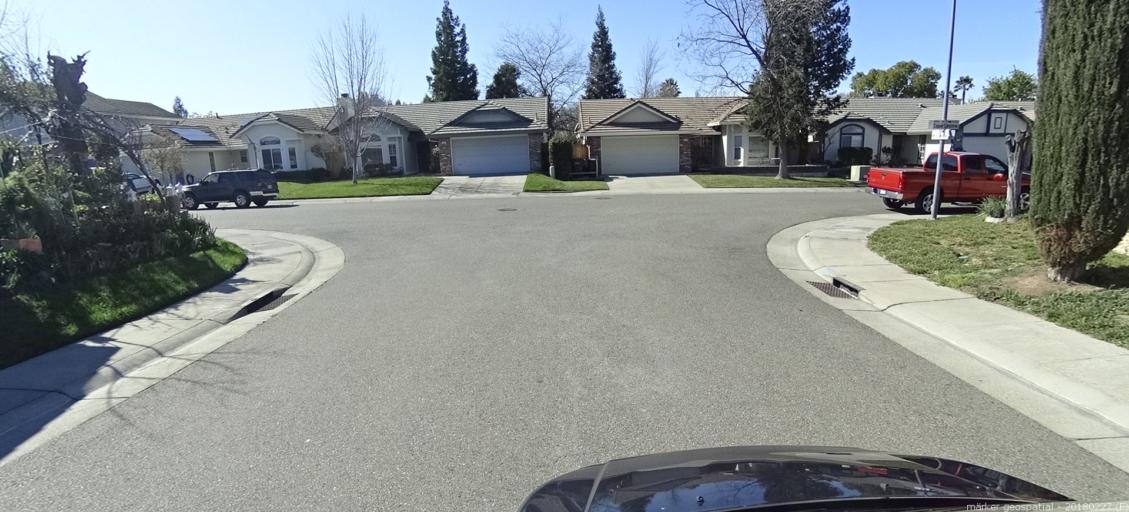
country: US
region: California
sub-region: Sacramento County
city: North Highlands
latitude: 38.7272
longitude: -121.3900
